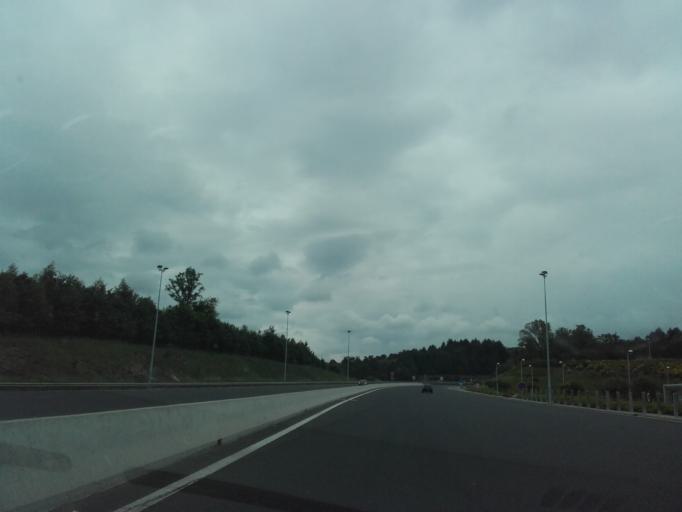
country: FR
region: Limousin
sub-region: Departement de la Correze
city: Saint-Mexant
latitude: 45.2844
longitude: 1.6178
